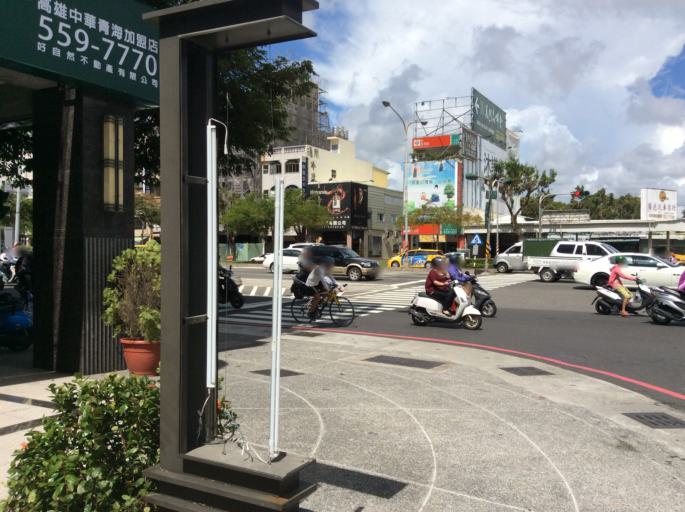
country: TW
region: Kaohsiung
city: Kaohsiung
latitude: 22.6513
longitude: 120.2917
